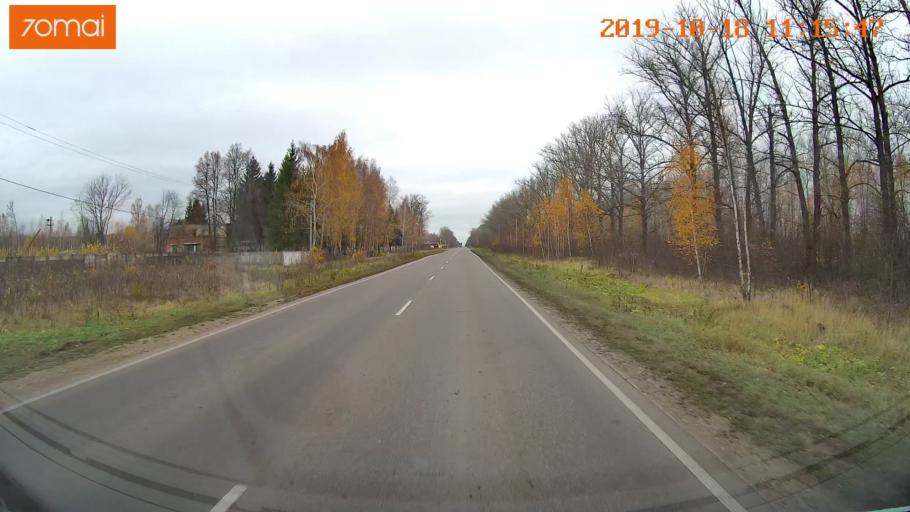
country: RU
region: Tula
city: Kimovsk
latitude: 53.9974
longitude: 38.5479
